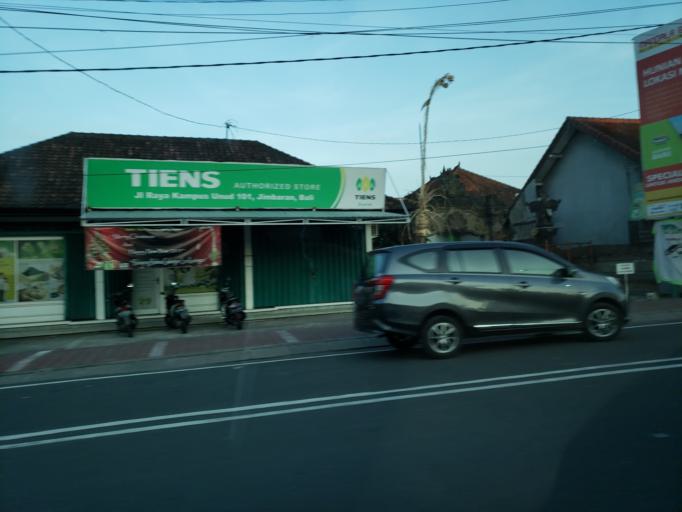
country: ID
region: Bali
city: Jimbaran
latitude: -8.7851
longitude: 115.1785
